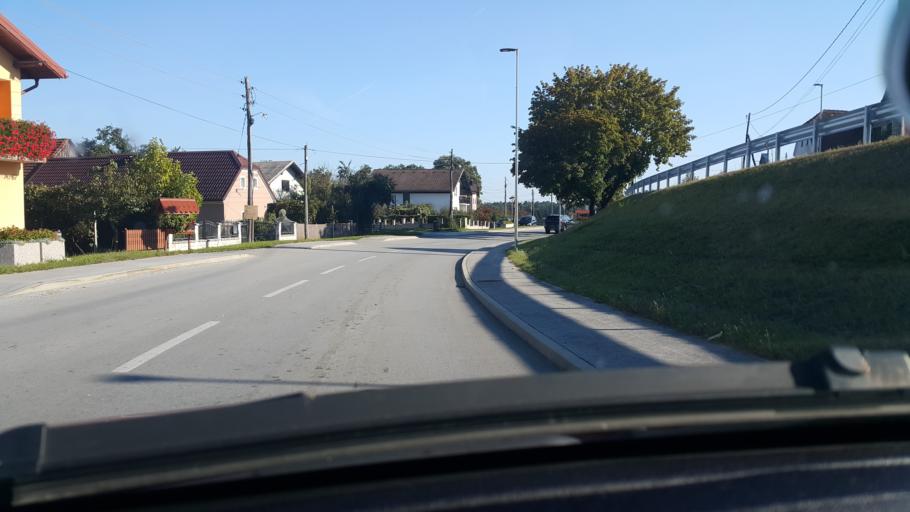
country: SI
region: Miklavz na Dravskem Polju
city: Miklavz na Dravskem Polju
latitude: 46.4796
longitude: 15.7048
